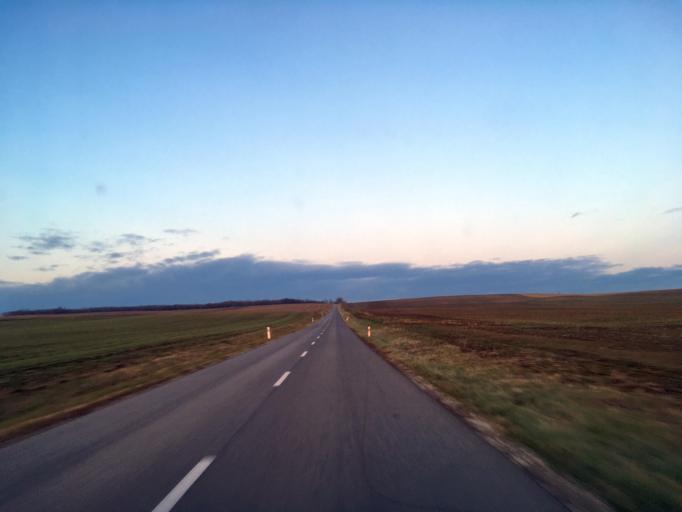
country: SK
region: Nitriansky
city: Svodin
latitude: 47.8528
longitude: 18.4449
